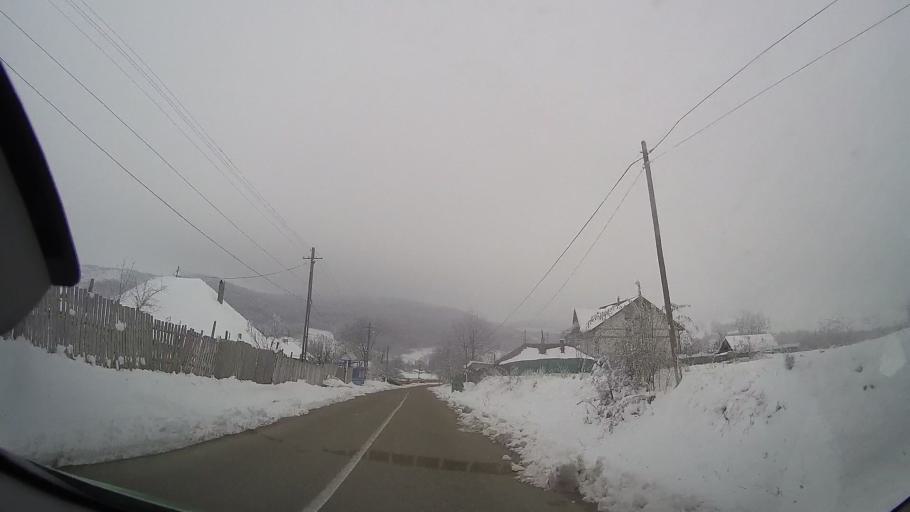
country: RO
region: Neamt
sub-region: Comuna Bozieni
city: Bozieni
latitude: 46.8377
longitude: 27.1662
